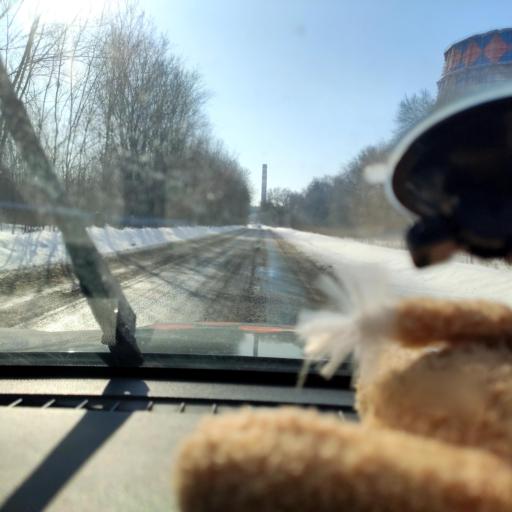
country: RU
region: Samara
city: Tol'yatti
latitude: 53.5770
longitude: 49.2552
